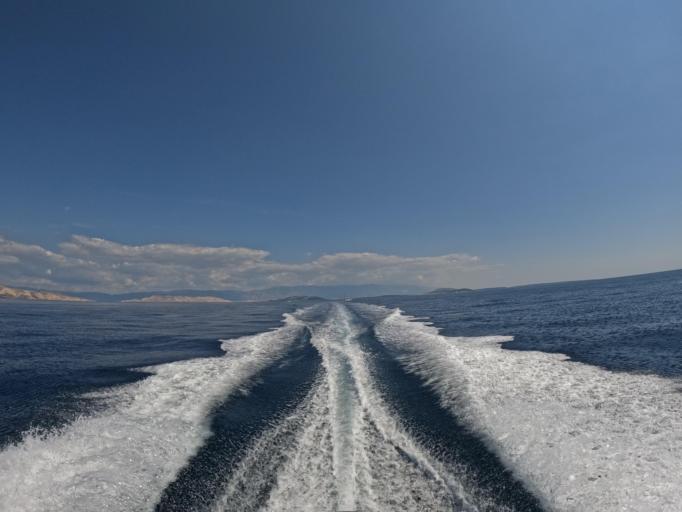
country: HR
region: Primorsko-Goranska
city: Punat
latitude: 44.9031
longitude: 14.6079
